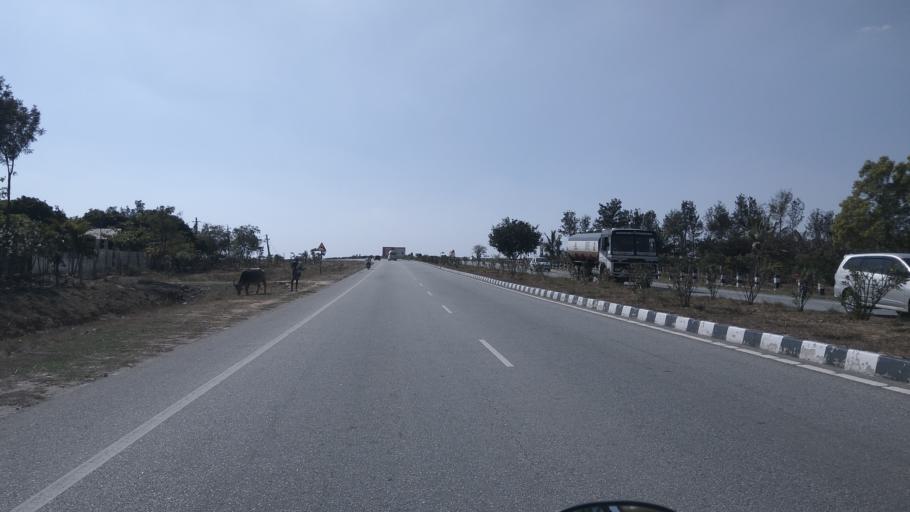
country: IN
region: Karnataka
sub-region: Kolar
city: Mulbagal
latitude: 13.1535
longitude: 78.3107
